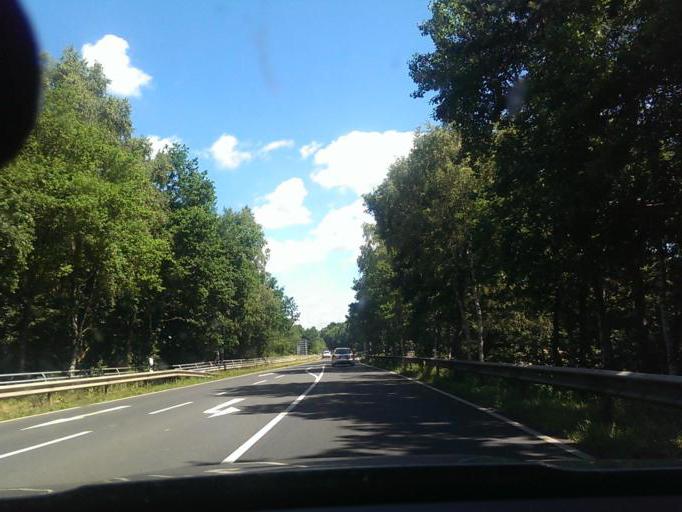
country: DE
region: Lower Saxony
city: Verden
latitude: 52.9605
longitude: 9.2462
